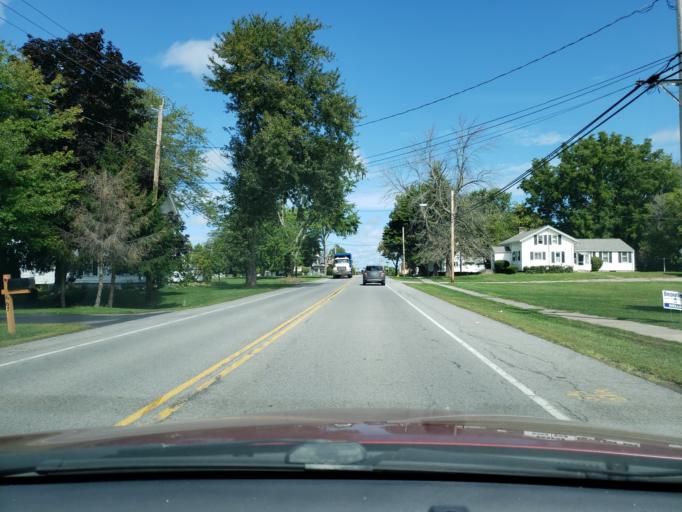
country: US
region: New York
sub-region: Monroe County
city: Greece
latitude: 43.2512
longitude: -77.7329
